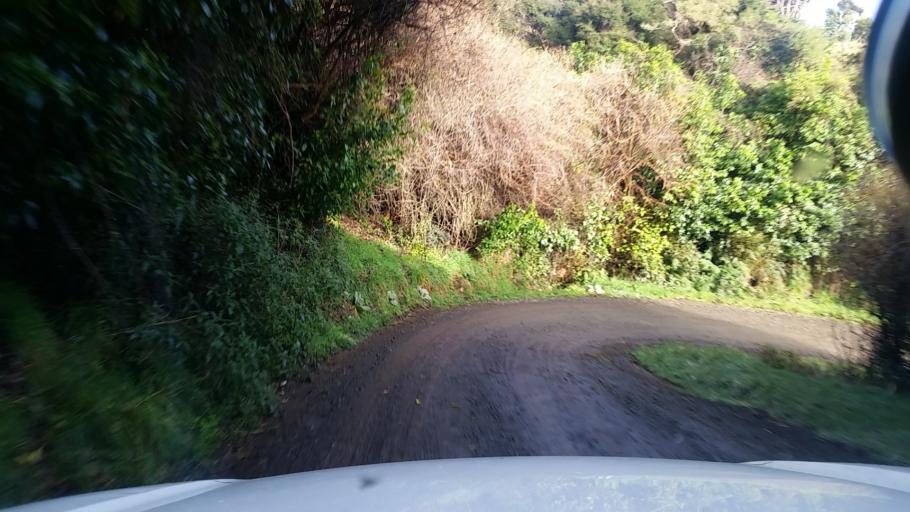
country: NZ
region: Canterbury
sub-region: Christchurch City
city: Christchurch
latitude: -43.7278
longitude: 172.8851
